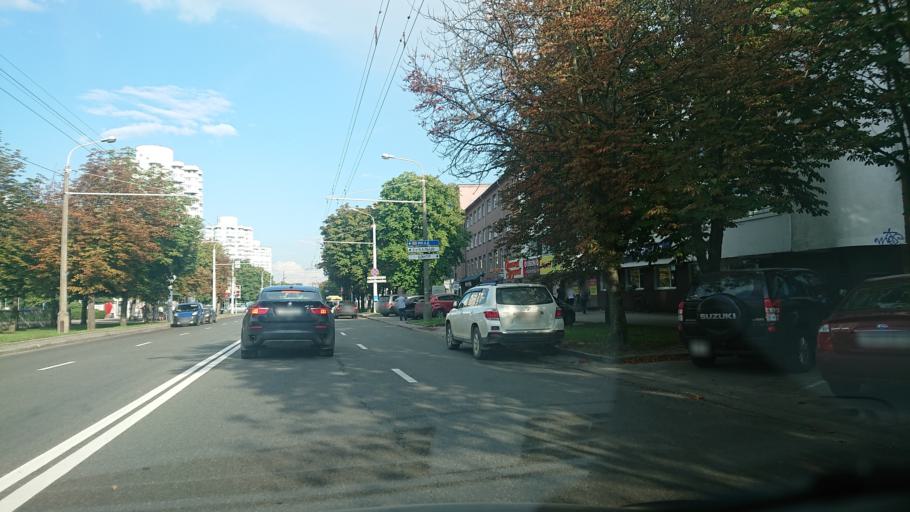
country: BY
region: Minsk
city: Minsk
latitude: 53.9217
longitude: 27.5658
